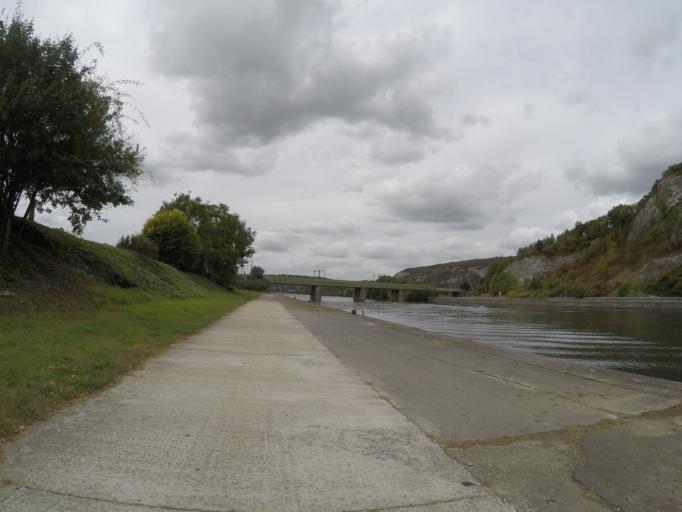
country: BE
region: Wallonia
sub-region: Province de Namur
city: Anhee
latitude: 50.3044
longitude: 4.8933
